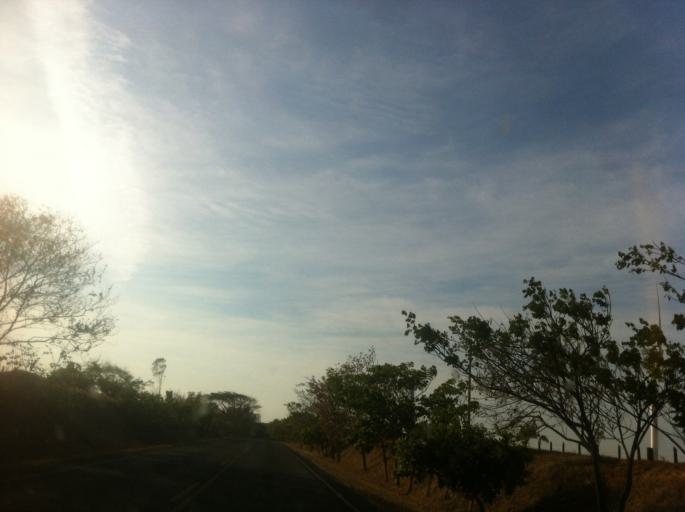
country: NI
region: Rivas
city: San Jorge
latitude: 11.3155
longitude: -85.7093
